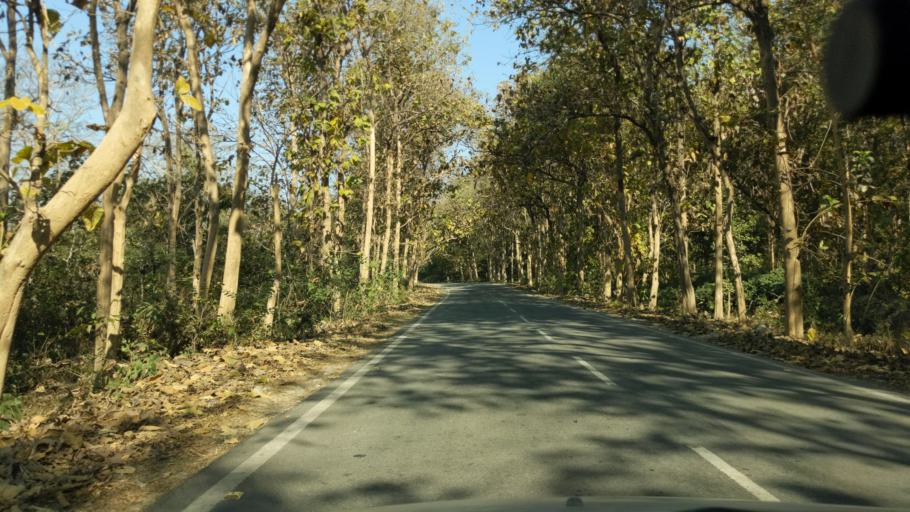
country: IN
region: Uttarakhand
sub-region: Naini Tal
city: Ramnagar
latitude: 29.3962
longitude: 79.1366
